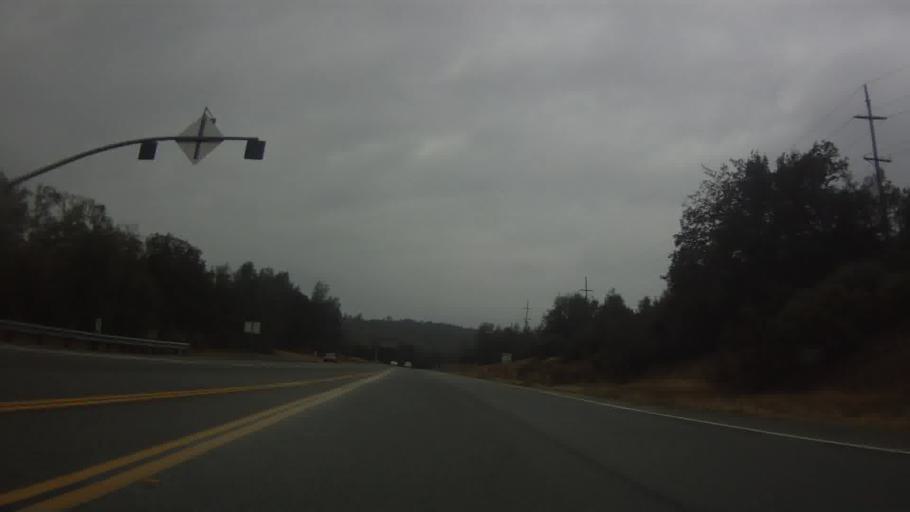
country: US
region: California
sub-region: Shasta County
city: Redding
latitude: 40.5829
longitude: -122.4306
